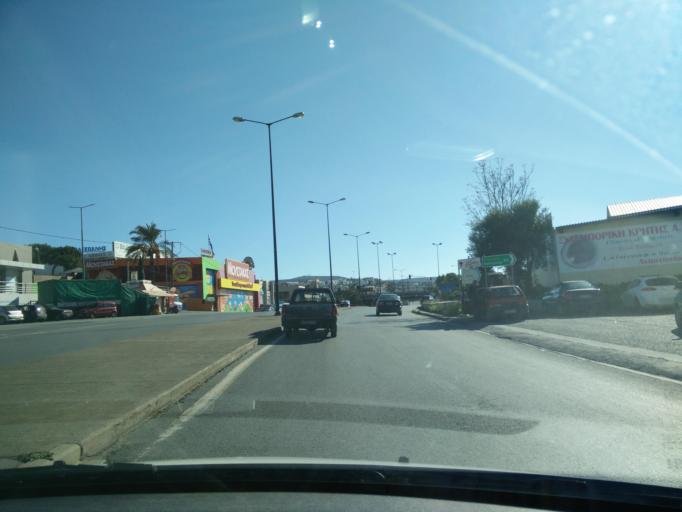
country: GR
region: Crete
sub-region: Nomos Irakleiou
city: Nea Alikarnassos
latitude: 35.3346
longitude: 25.1580
